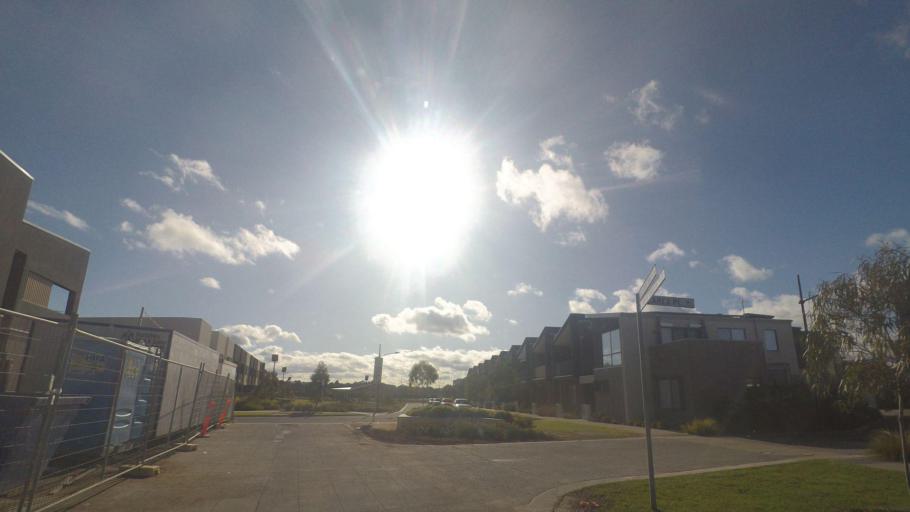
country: AU
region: Victoria
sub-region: Knox
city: Scoresby
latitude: -37.9153
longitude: 145.2301
